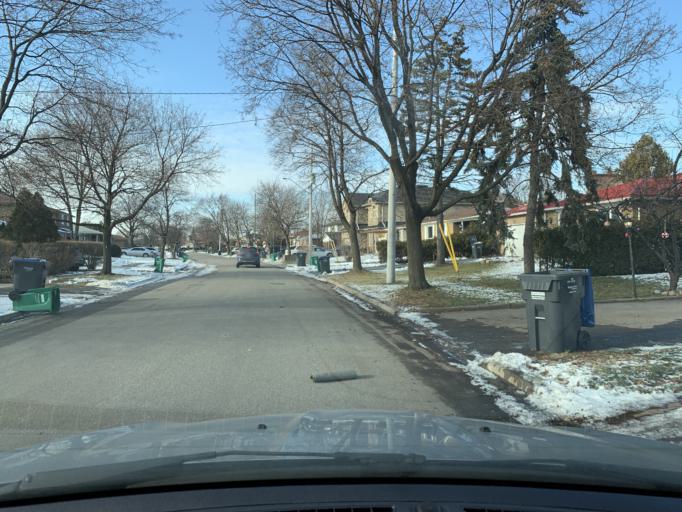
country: CA
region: Ontario
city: Etobicoke
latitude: 43.7240
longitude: -79.6270
